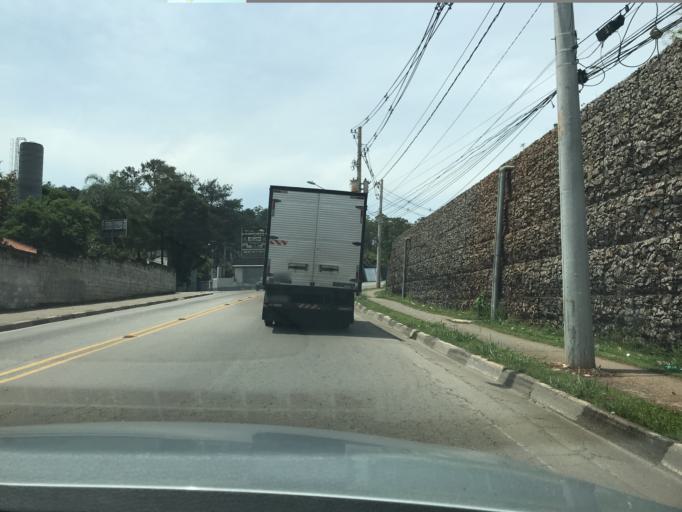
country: BR
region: Sao Paulo
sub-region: Cajamar
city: Cajamar
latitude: -23.4093
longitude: -46.8242
